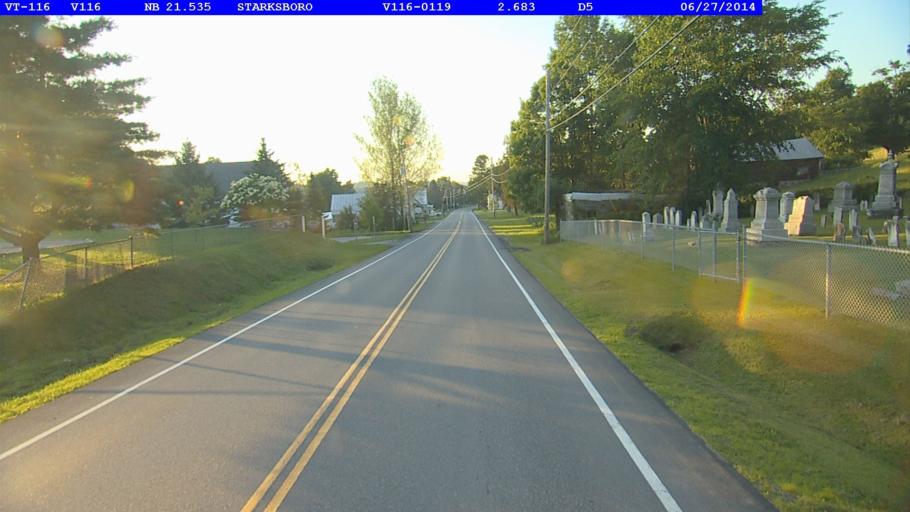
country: US
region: Vermont
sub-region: Addison County
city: Bristol
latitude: 44.2232
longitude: -73.0565
